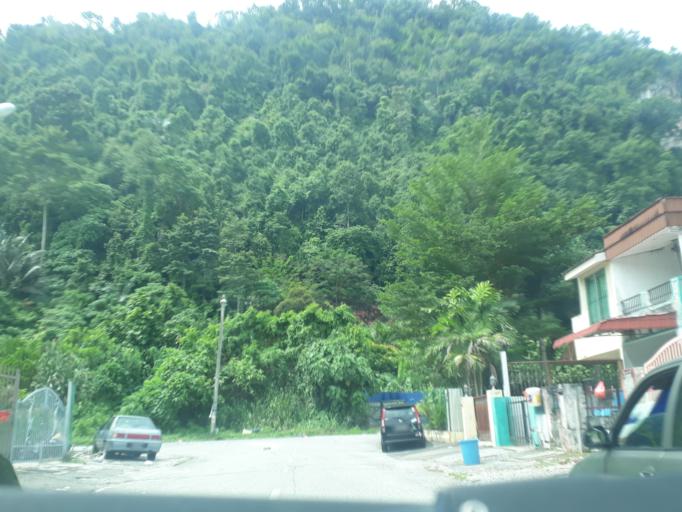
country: MY
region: Perak
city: Ipoh
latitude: 4.5934
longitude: 101.1336
